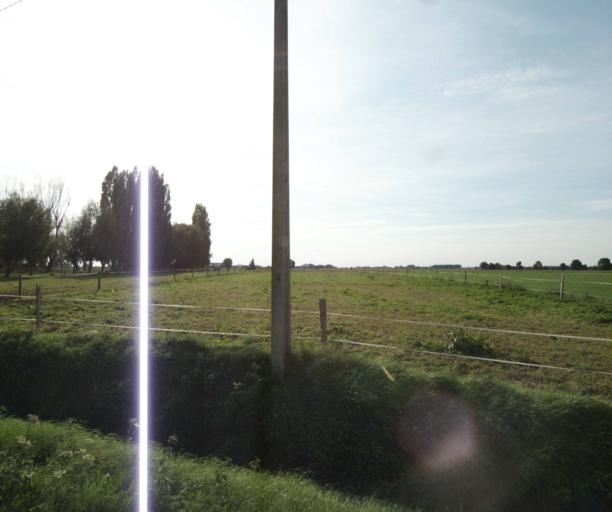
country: FR
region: Nord-Pas-de-Calais
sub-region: Departement du Nord
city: Fournes-en-Weppes
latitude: 50.5945
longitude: 2.8842
